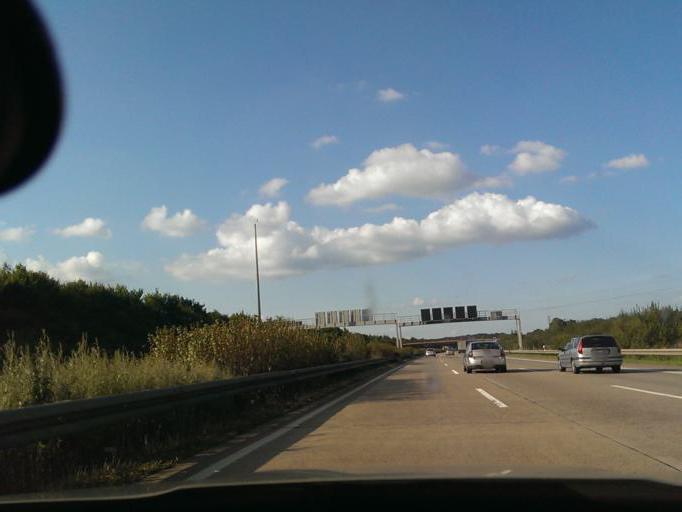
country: DE
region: Lower Saxony
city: Laatzen
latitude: 52.3239
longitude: 9.8638
